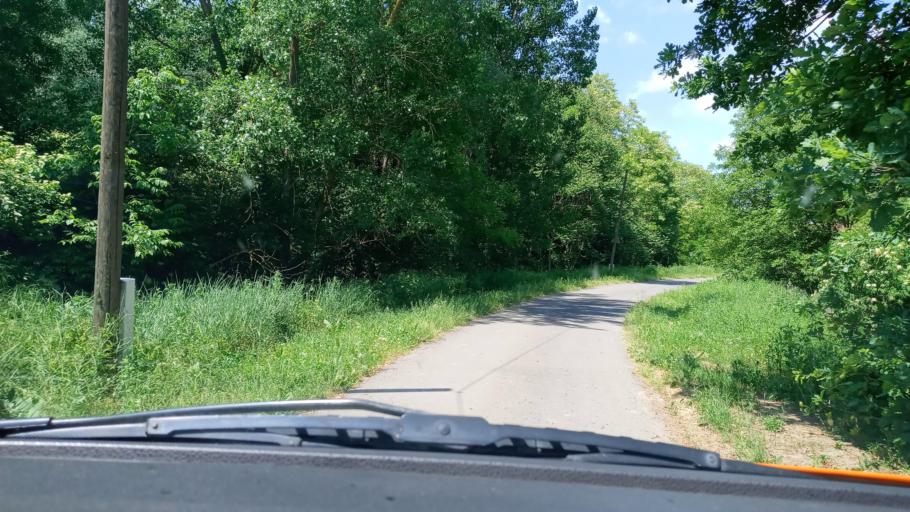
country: HR
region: Osjecko-Baranjska
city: Viljevo
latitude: 45.8083
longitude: 18.1169
